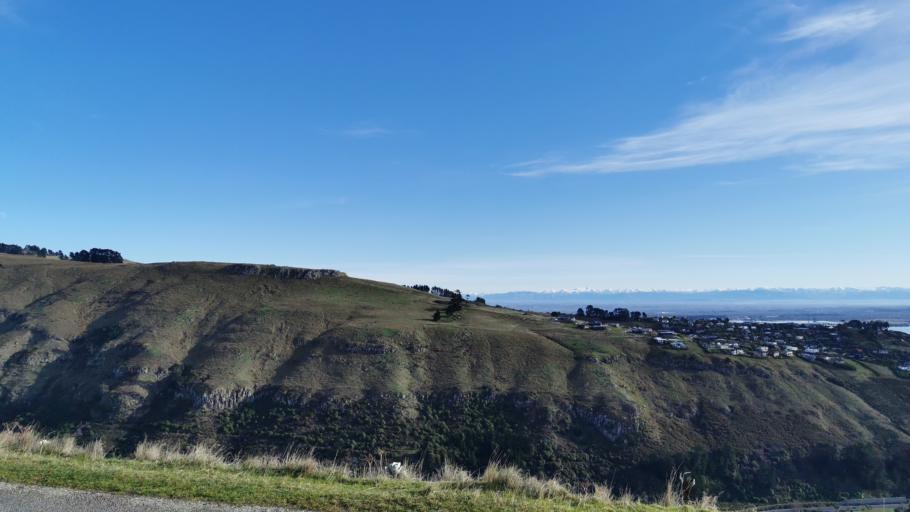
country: NZ
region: Canterbury
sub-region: Christchurch City
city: Christchurch
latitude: -43.5842
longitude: 172.7625
